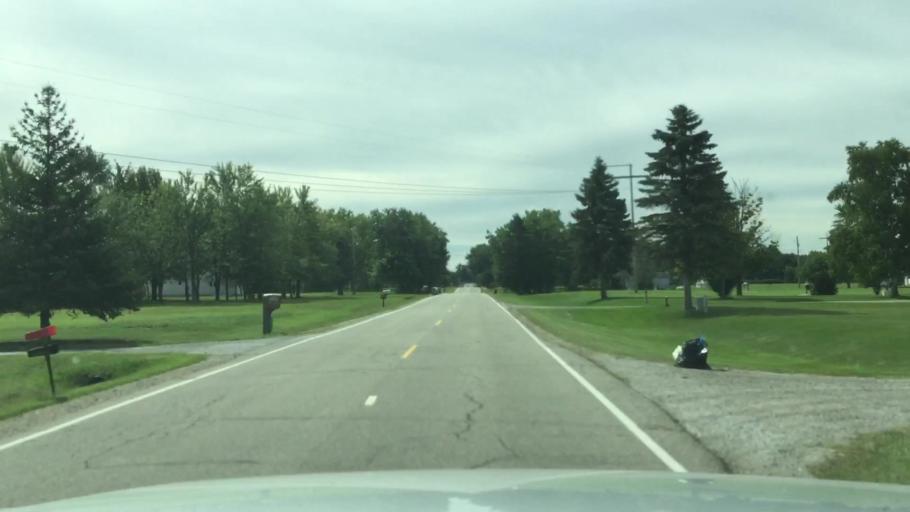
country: US
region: Michigan
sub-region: Genesee County
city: Montrose
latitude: 43.1090
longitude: -83.9879
